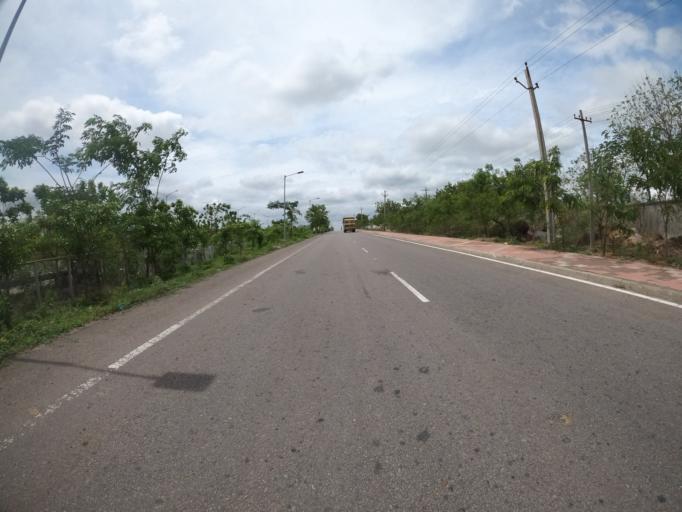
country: IN
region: Telangana
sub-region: Hyderabad
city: Hyderabad
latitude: 17.2906
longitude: 78.3812
